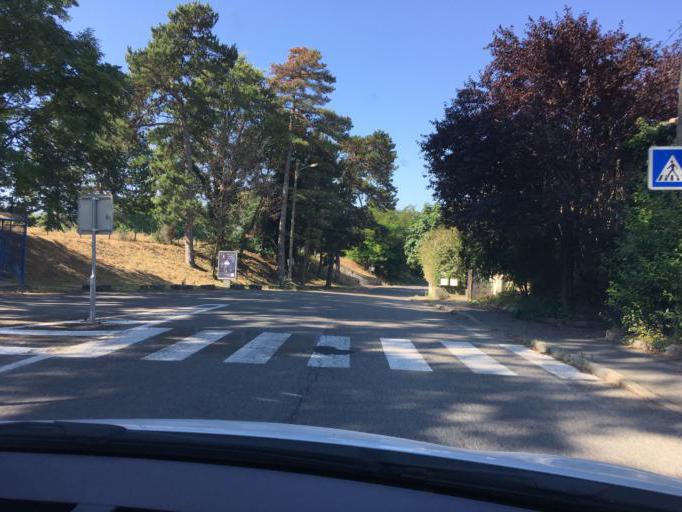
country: FR
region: Provence-Alpes-Cote d'Azur
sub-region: Departement des Alpes-de-Haute-Provence
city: Peyruis
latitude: 44.0326
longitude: 5.9481
